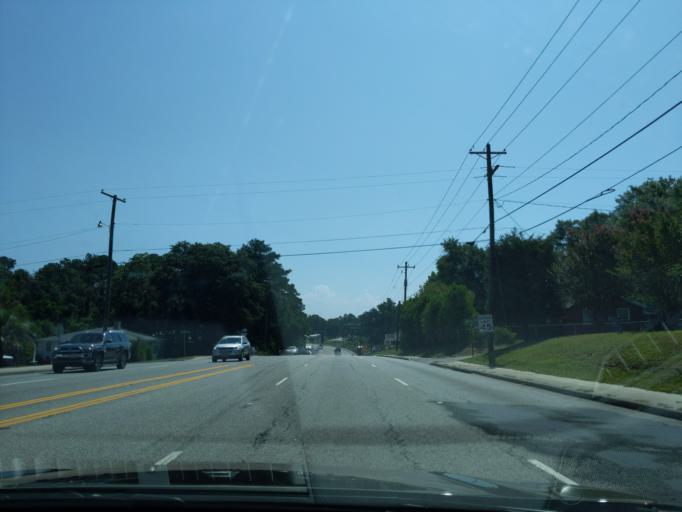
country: US
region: South Carolina
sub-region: Lexington County
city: Oak Grove
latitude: 33.9718
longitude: -81.1425
